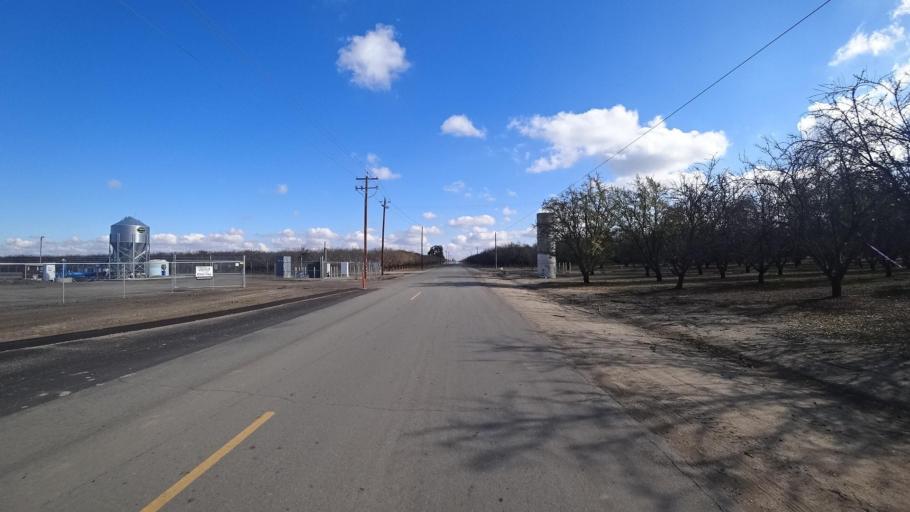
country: US
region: California
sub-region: Kern County
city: McFarland
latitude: 35.6887
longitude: -119.3038
